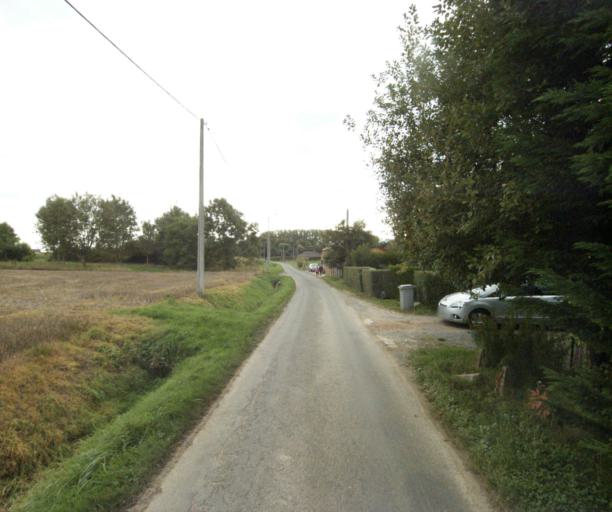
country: FR
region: Nord-Pas-de-Calais
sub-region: Departement du Nord
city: Ennetieres-en-Weppes
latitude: 50.6392
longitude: 2.9463
